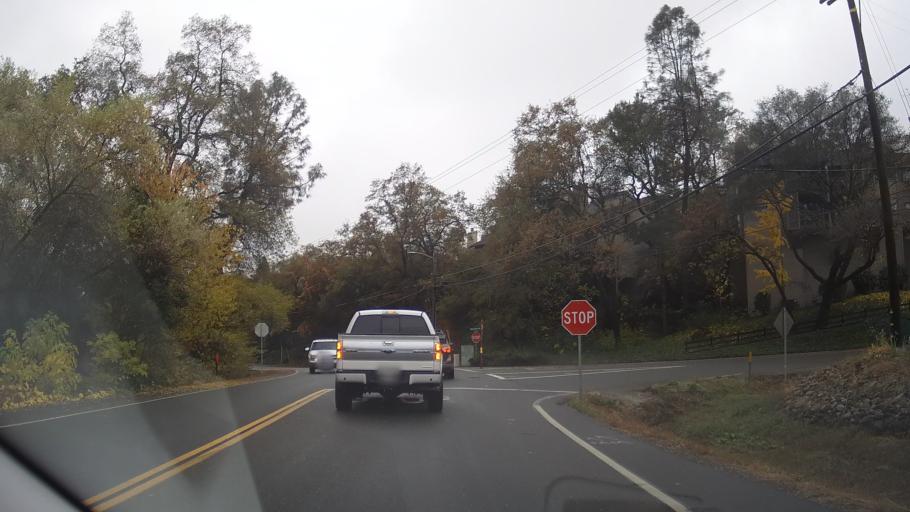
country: US
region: California
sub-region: Placer County
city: Auburn
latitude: 38.9144
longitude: -121.0739
